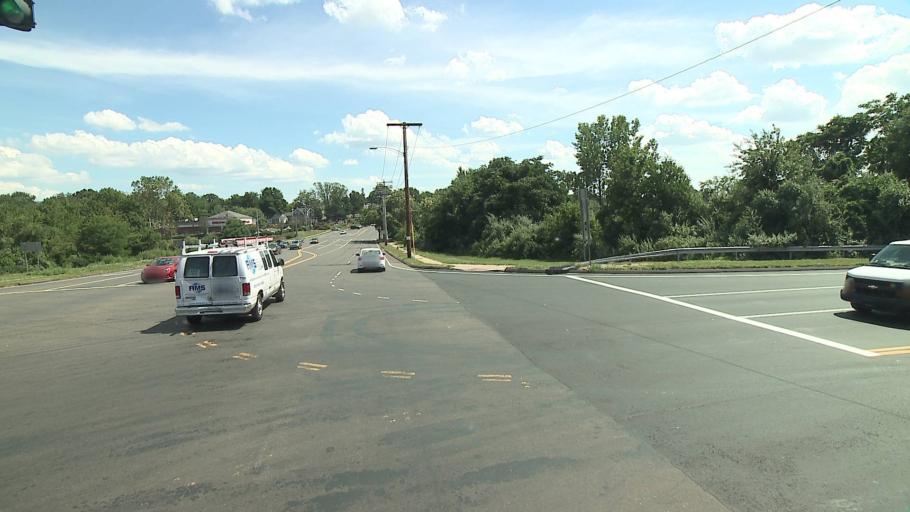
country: US
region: Connecticut
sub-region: Fairfield County
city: Trumbull
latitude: 41.2314
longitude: -73.1557
